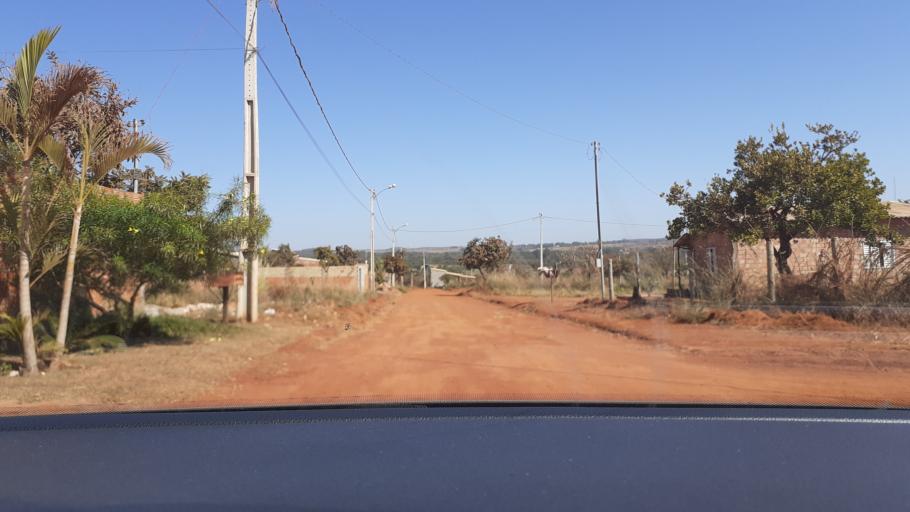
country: BR
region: Goias
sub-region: Aparecida De Goiania
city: Aparecida de Goiania
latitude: -16.8900
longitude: -49.2566
